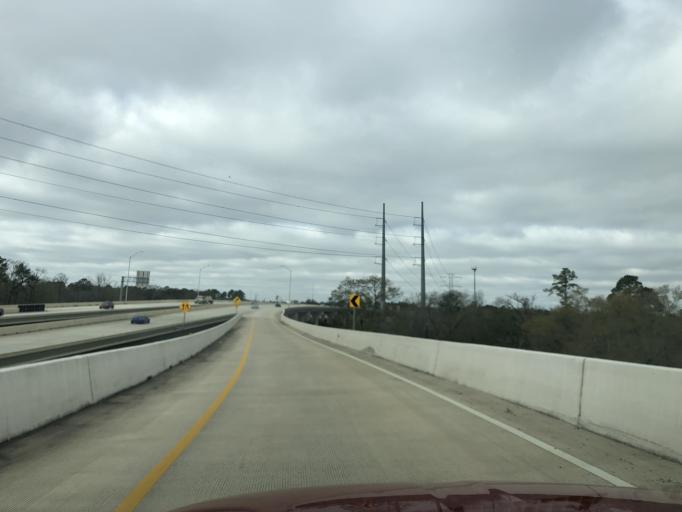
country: US
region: Texas
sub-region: Harris County
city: Spring
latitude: 30.0937
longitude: -95.4171
